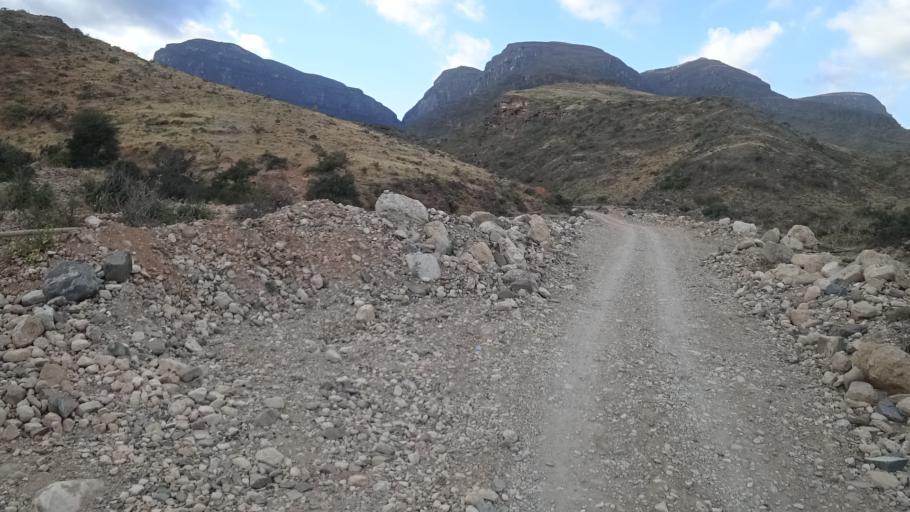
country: OM
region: Zufar
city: Salalah
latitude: 16.9957
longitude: 53.8460
